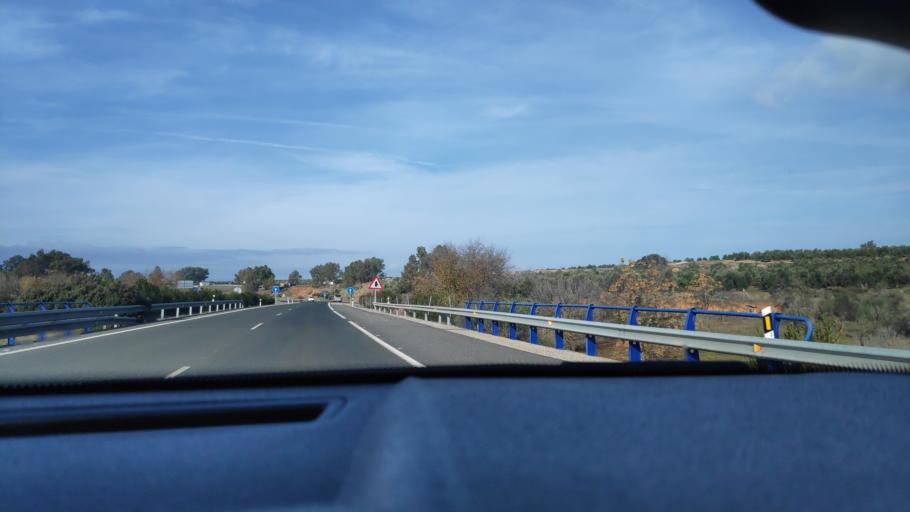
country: ES
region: Andalusia
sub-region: Provincia de Jaen
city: Linares
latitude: 38.0931
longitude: -3.6808
